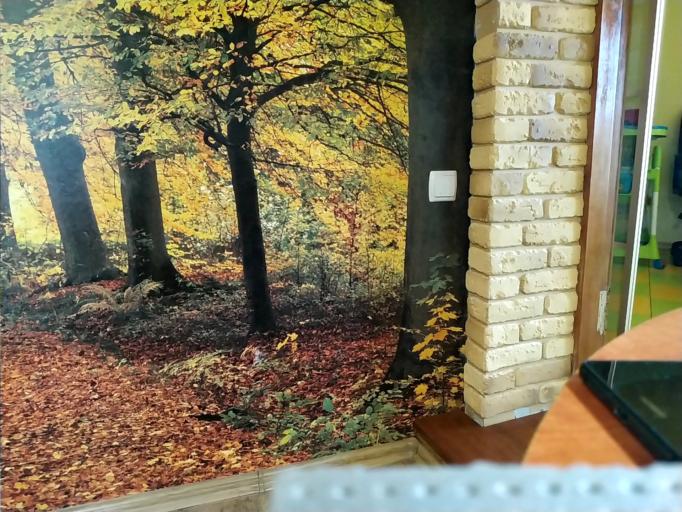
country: RU
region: Kaluga
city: Iznoski
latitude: 54.8578
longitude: 35.4448
